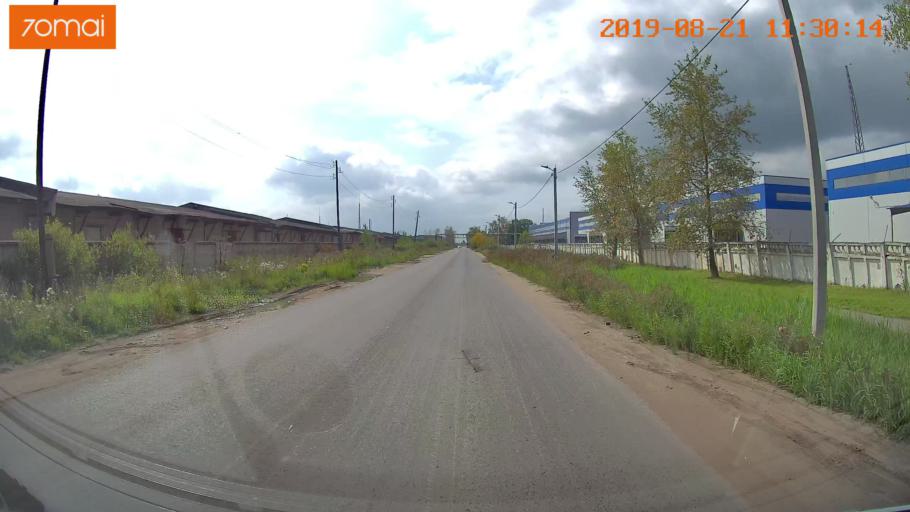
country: RU
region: Ivanovo
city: Novo-Talitsy
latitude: 56.9941
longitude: 40.9115
